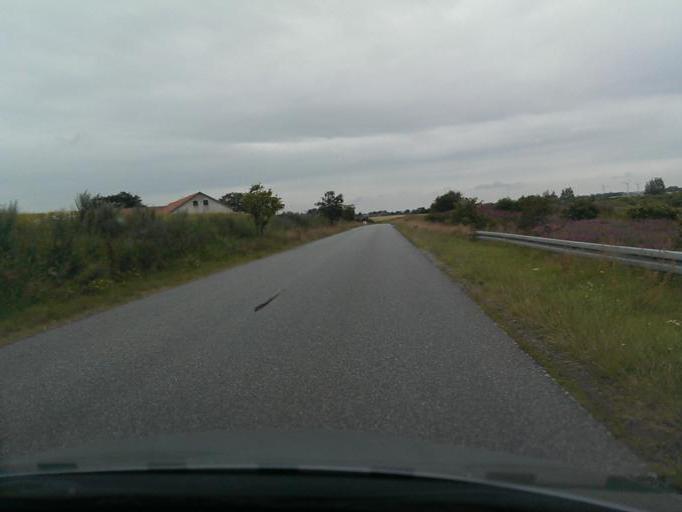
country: DK
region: North Denmark
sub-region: Hjorring Kommune
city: Vra
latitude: 57.3550
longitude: 9.9297
